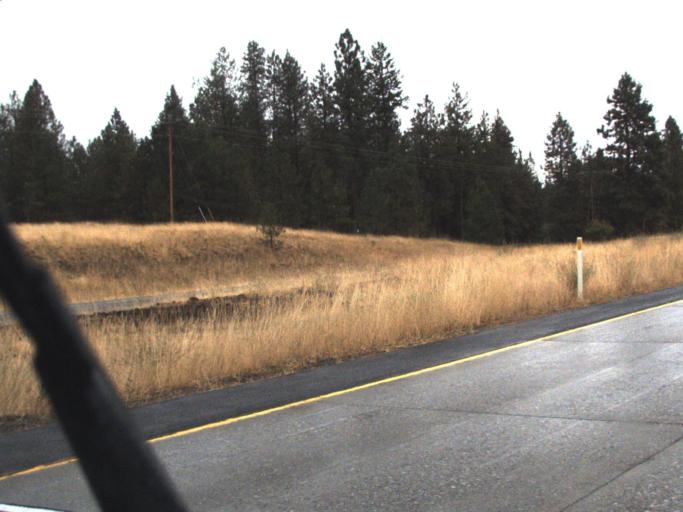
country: US
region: Washington
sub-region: Spokane County
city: Spokane
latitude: 47.5343
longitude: -117.4007
